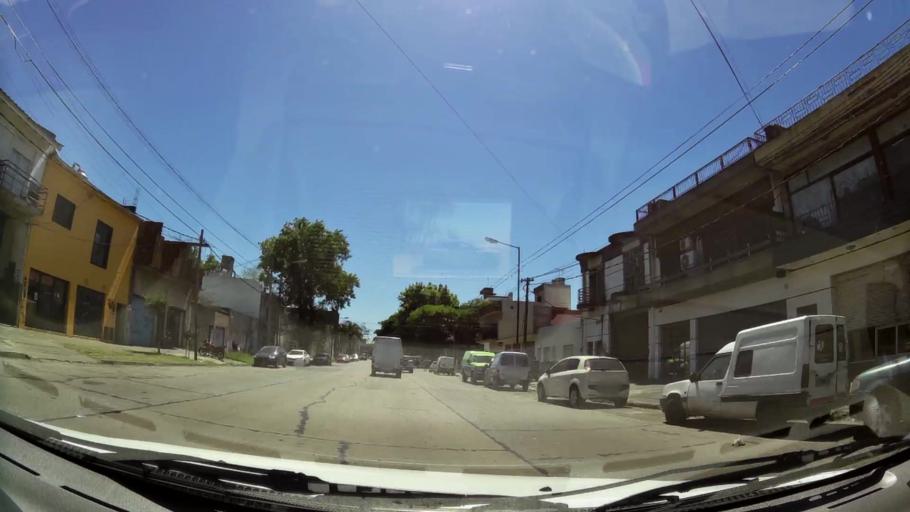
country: AR
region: Buenos Aires
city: Caseros
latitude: -34.5873
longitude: -58.5616
